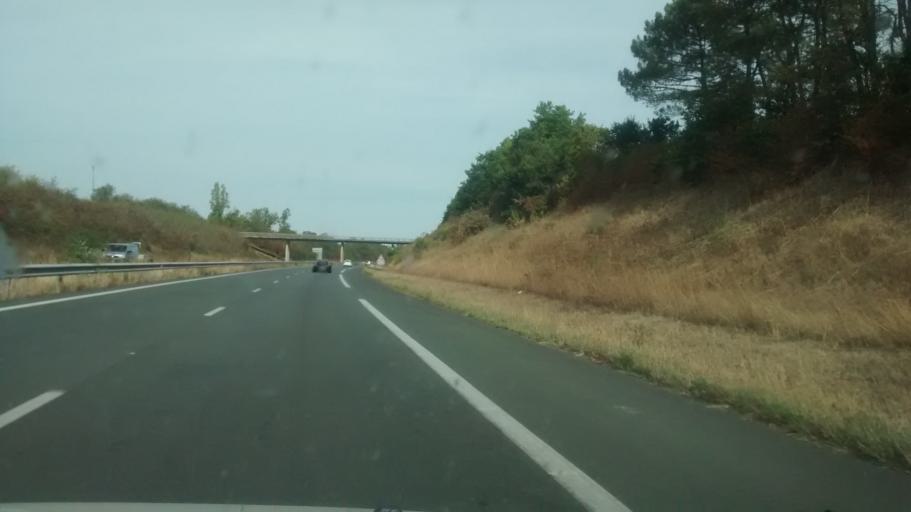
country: FR
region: Aquitaine
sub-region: Departement du Lot-et-Garonne
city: Fourques-sur-Garonne
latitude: 44.4528
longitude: 0.0887
